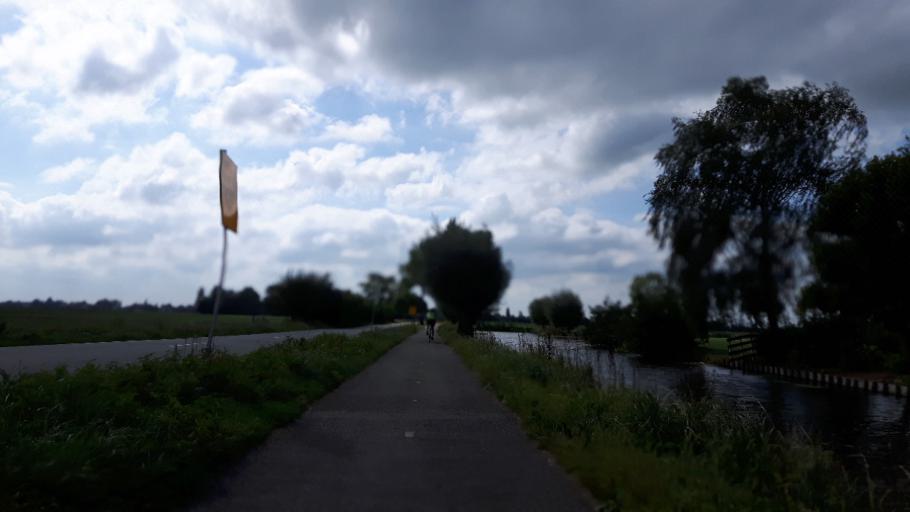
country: NL
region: Utrecht
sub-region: Gemeente Woerden
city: Woerden
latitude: 52.1251
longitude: 4.8513
